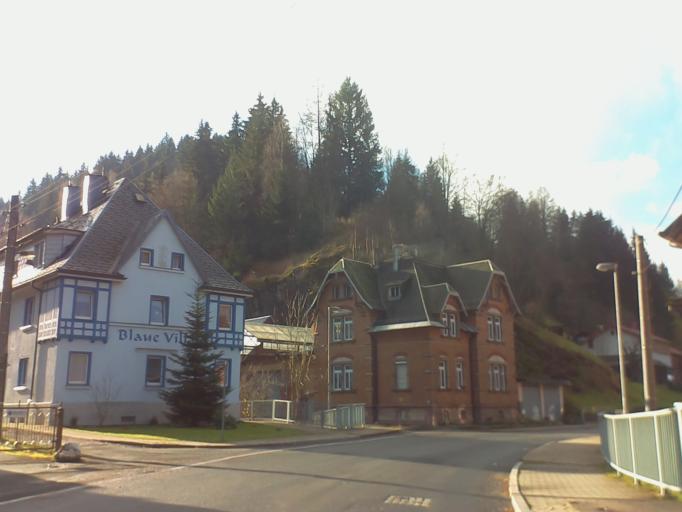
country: DE
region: Thuringia
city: Katzhutte
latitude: 50.5592
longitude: 11.0607
